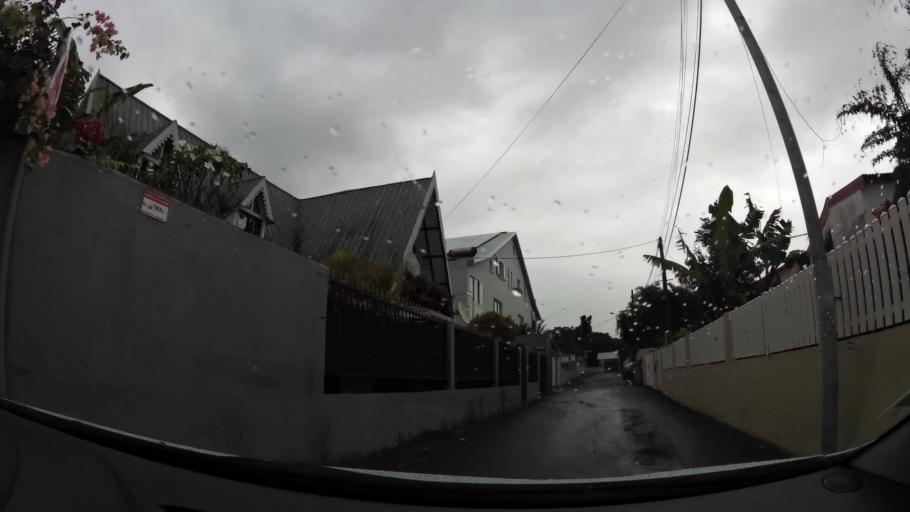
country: RE
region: Reunion
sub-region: Reunion
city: Saint-Andre
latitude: -20.9477
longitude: 55.6497
